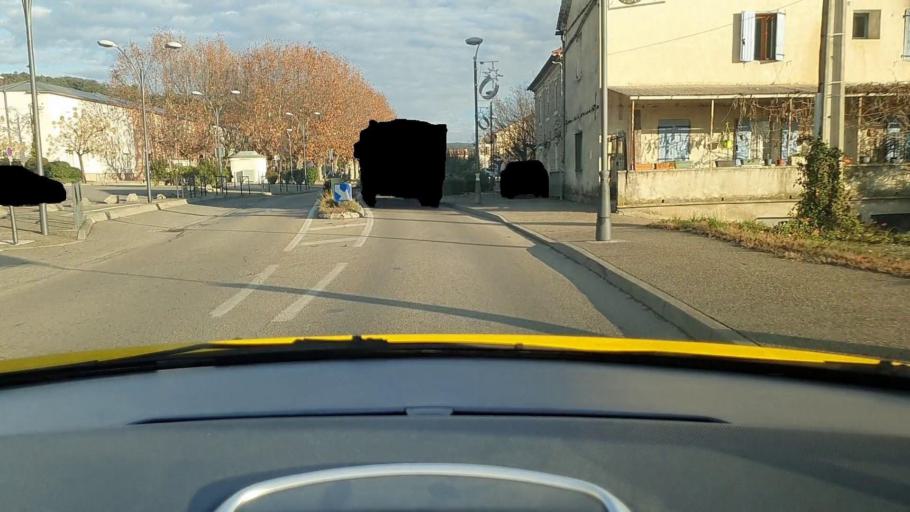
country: FR
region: Languedoc-Roussillon
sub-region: Departement du Gard
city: Saint-Martin-de-Valgalgues
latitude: 44.1606
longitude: 4.0831
